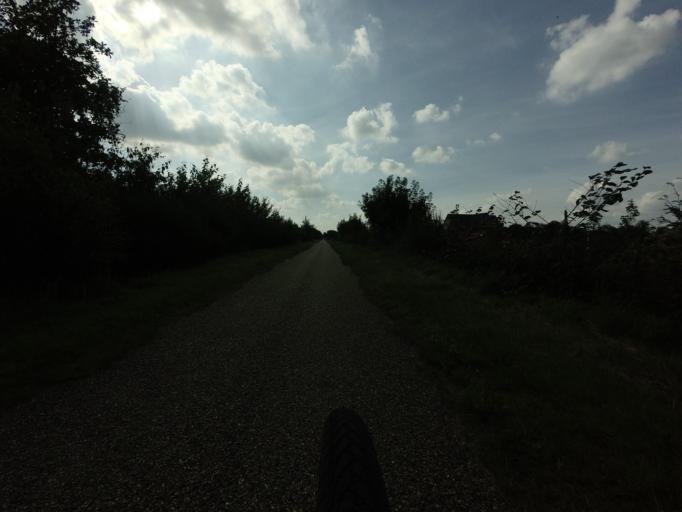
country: DK
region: Central Jutland
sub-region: Herning Kommune
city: Sunds
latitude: 56.2322
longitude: 9.0826
